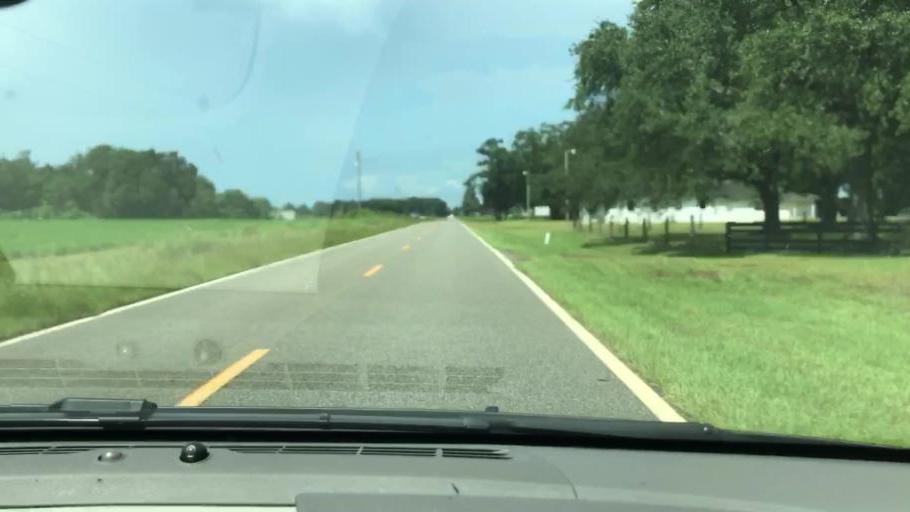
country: US
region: Georgia
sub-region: Seminole County
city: Donalsonville
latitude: 31.1095
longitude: -84.9959
